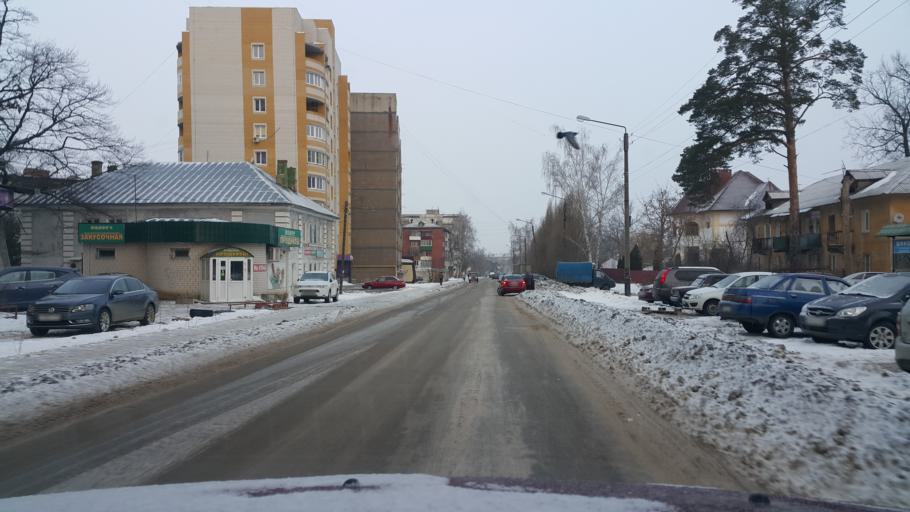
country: RU
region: Tambov
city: Kotovsk
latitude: 52.5781
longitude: 41.5129
